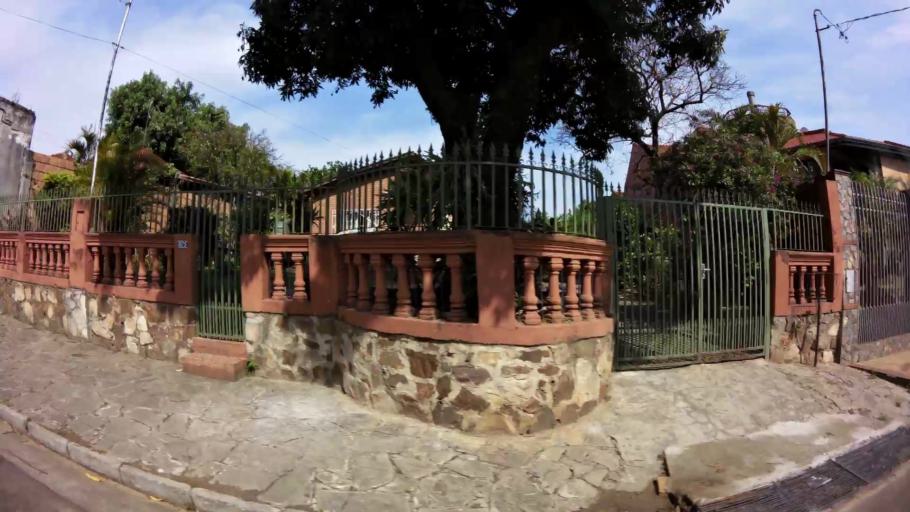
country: PY
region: Central
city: Fernando de la Mora
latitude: -25.2676
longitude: -57.5492
